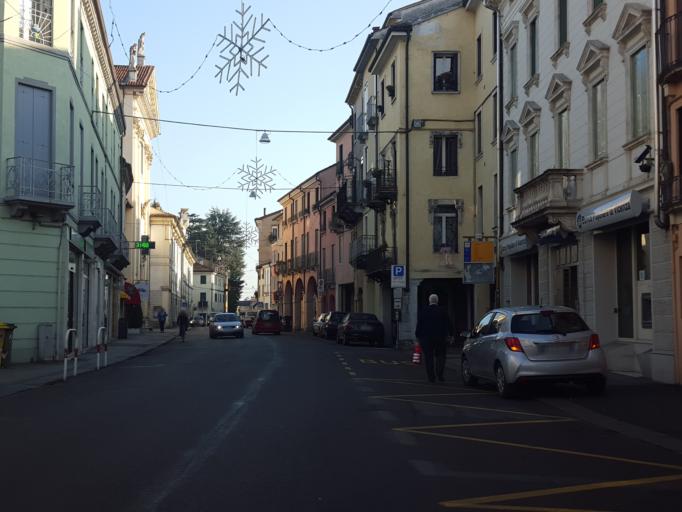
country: IT
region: Veneto
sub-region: Provincia di Vicenza
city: Vicenza
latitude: 45.5485
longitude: 11.5563
